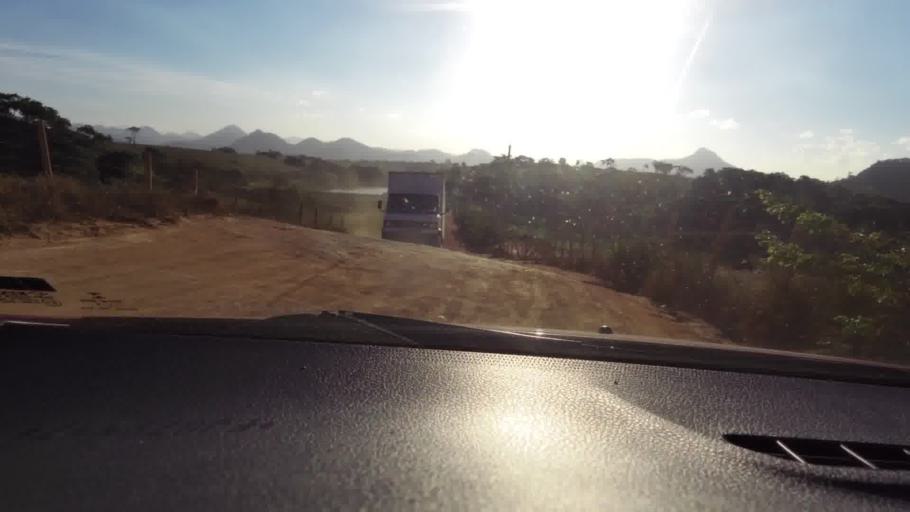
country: BR
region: Espirito Santo
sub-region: Guarapari
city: Guarapari
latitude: -20.5387
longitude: -40.4350
